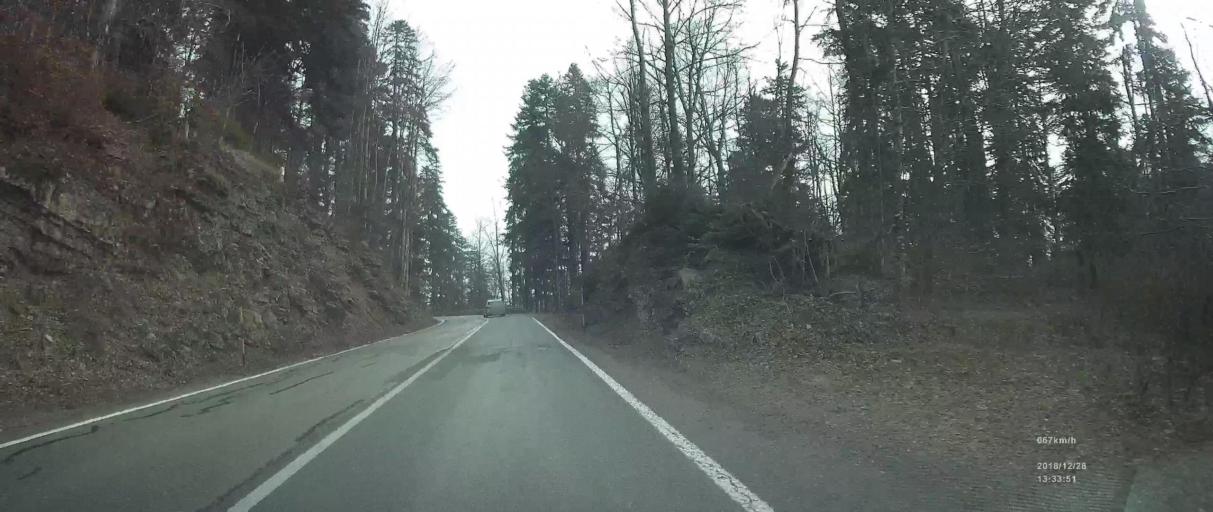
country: HR
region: Primorsko-Goranska
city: Hreljin
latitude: 45.3413
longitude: 14.6839
